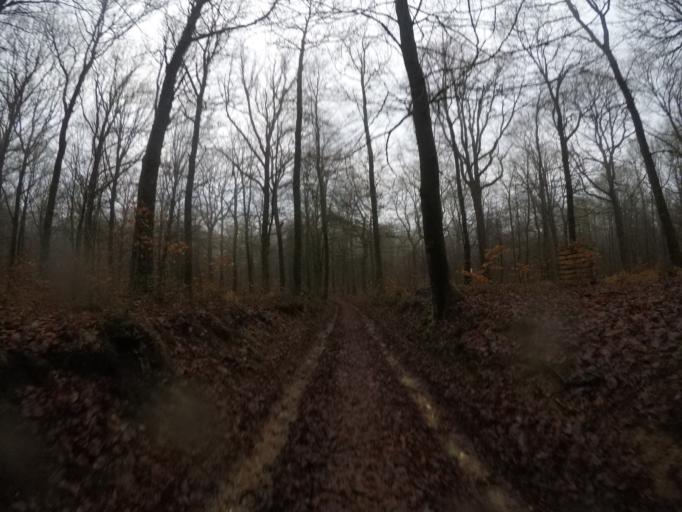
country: BE
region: Wallonia
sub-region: Province du Luxembourg
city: Leglise
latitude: 49.8154
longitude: 5.6004
